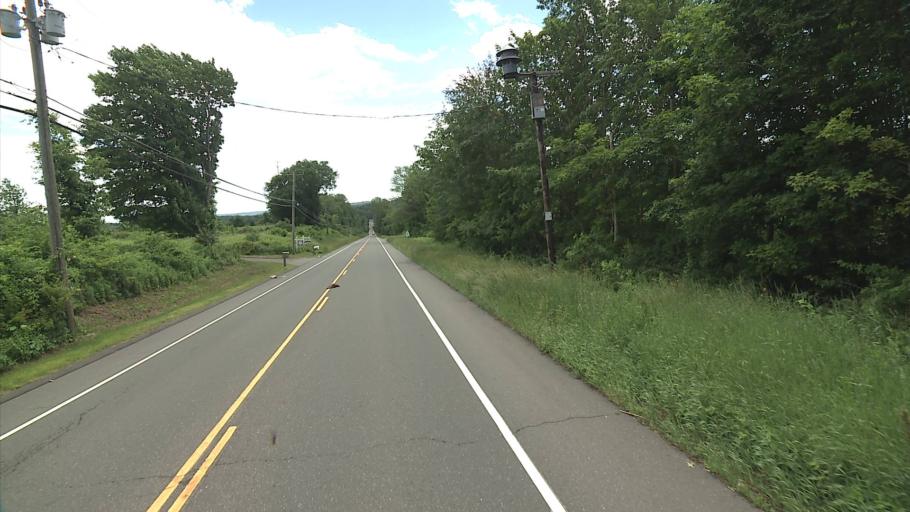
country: US
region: Connecticut
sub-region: Litchfield County
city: Watertown
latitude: 41.6222
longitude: -73.1324
